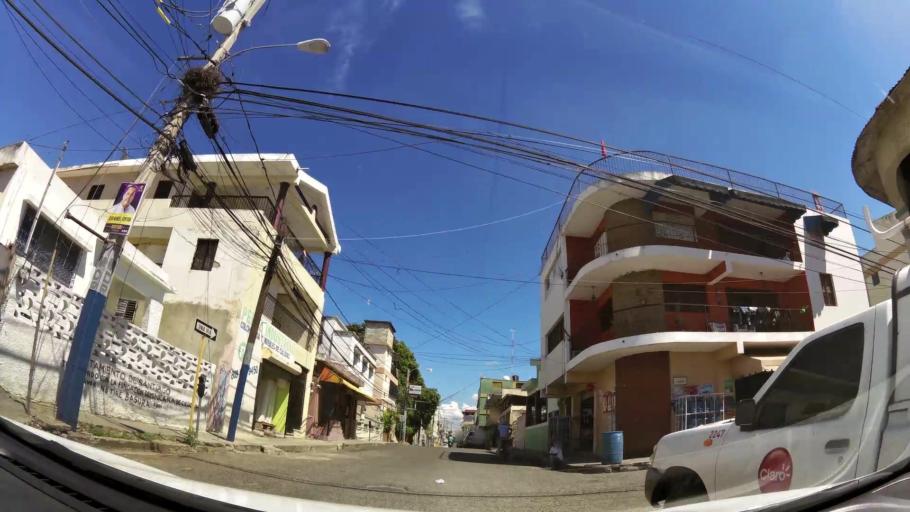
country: DO
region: Santiago
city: Santiago de los Caballeros
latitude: 19.4525
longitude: -70.7086
